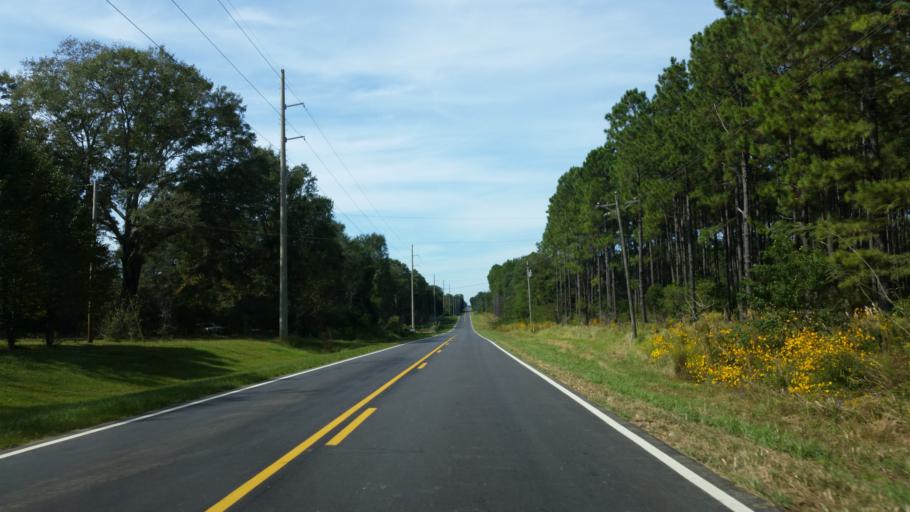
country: US
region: Alabama
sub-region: Baldwin County
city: Loxley
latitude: 30.6332
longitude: -87.6943
